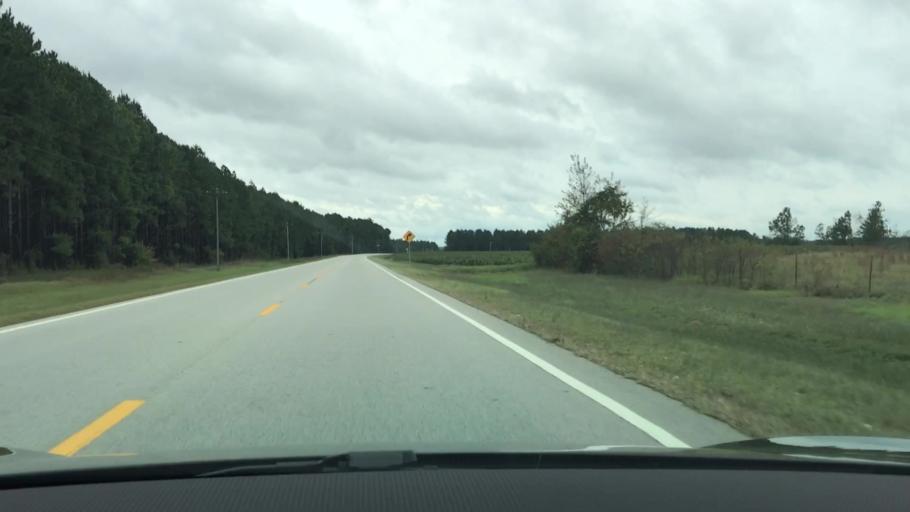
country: US
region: Georgia
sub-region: Glascock County
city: Gibson
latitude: 33.2881
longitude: -82.5080
